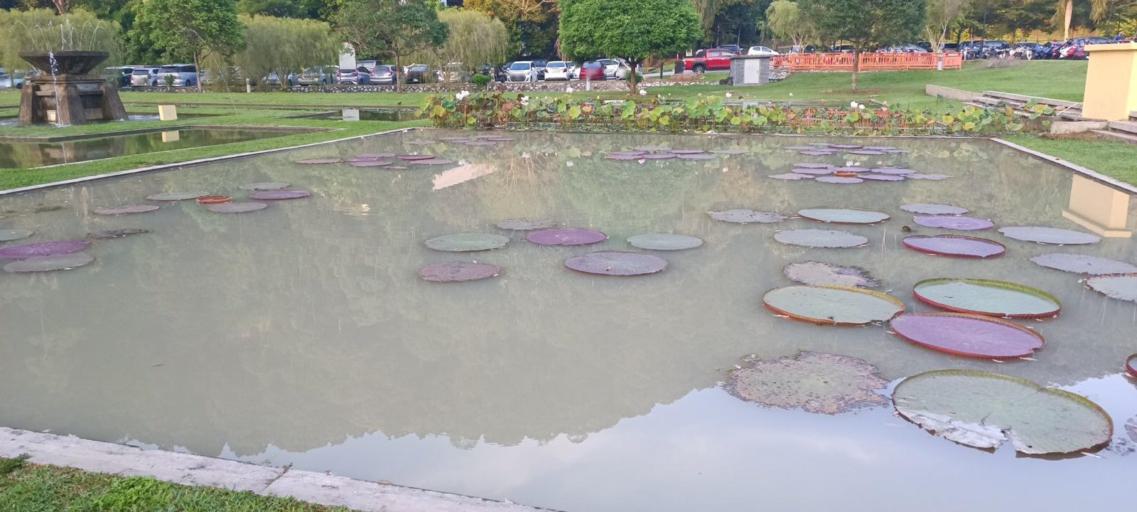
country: MY
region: Penang
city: Tanjung Tokong
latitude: 5.4373
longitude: 100.2911
